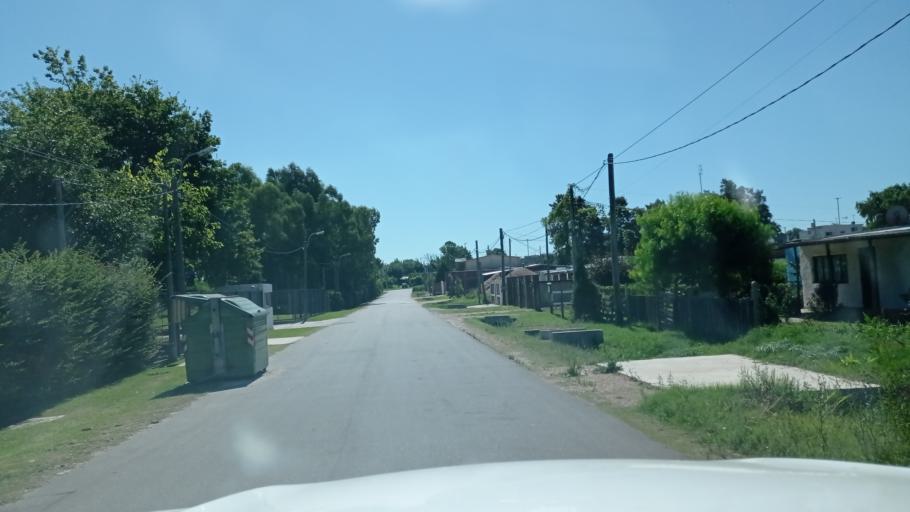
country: UY
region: Canelones
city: La Paz
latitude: -34.8289
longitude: -56.2463
